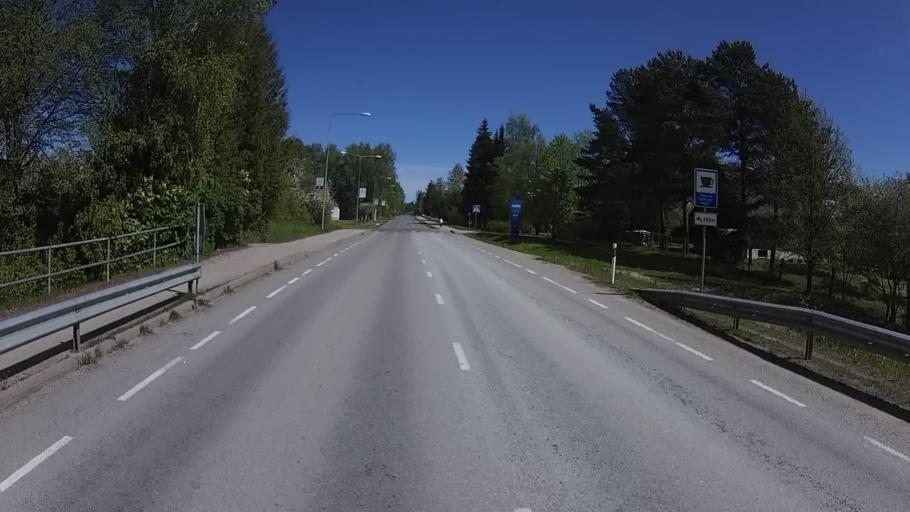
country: EE
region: Polvamaa
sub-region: Raepina vald
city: Rapina
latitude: 58.0927
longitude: 27.4602
